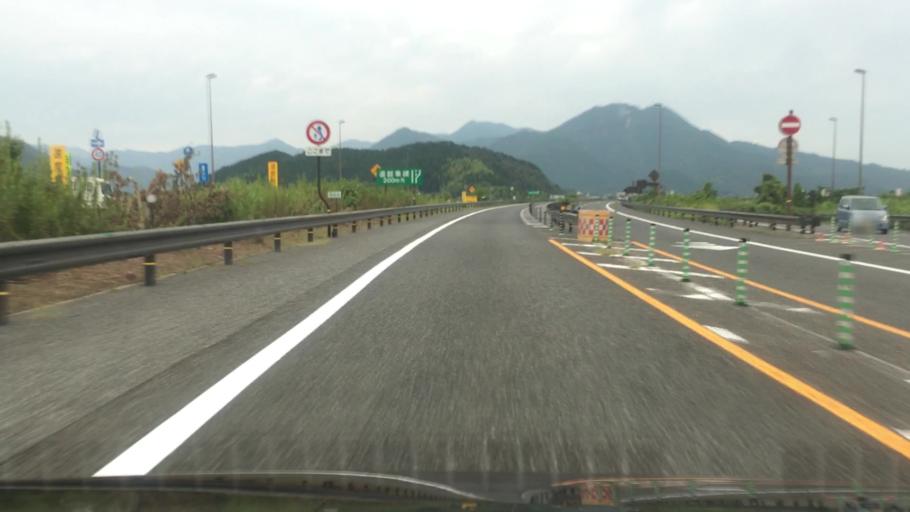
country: JP
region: Kyoto
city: Fukuchiyama
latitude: 35.1612
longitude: 135.0472
